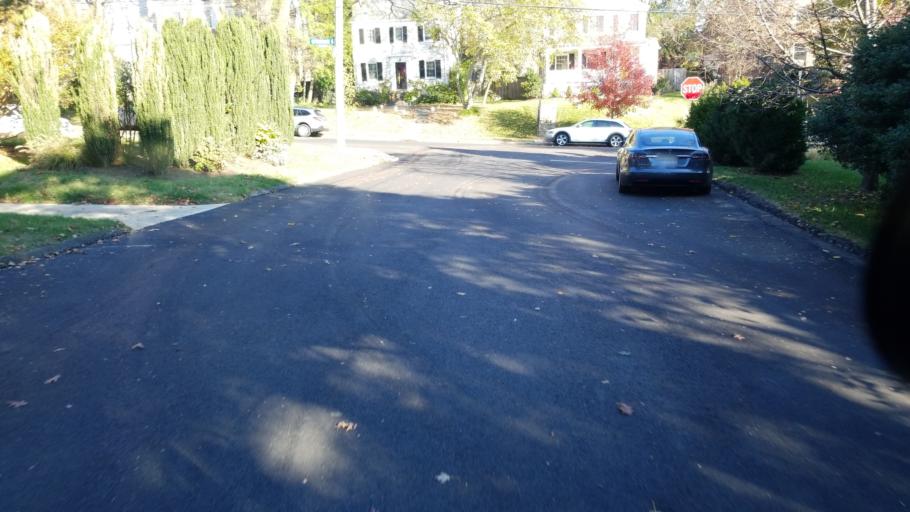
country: US
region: Maryland
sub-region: Montgomery County
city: Chevy Chase
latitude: 38.9694
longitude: -77.0585
